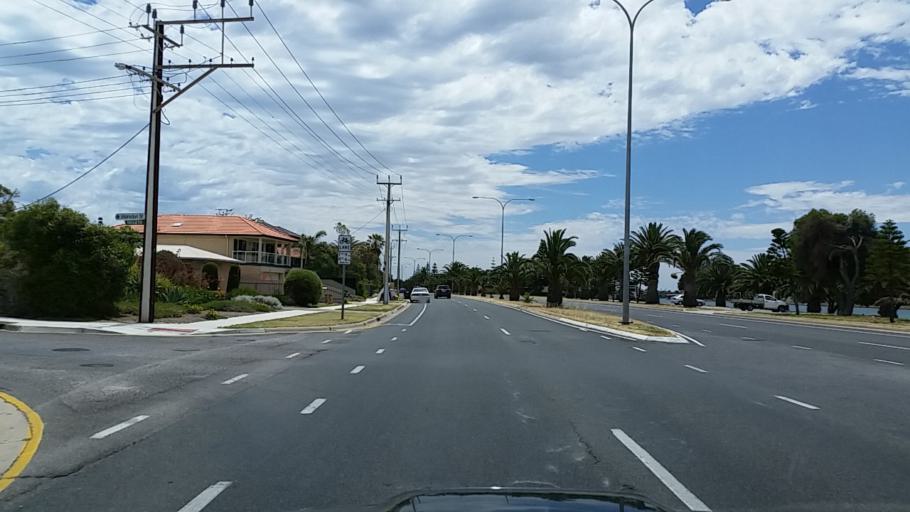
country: AU
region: South Australia
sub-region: Charles Sturt
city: Grange
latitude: -34.8871
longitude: 138.4868
